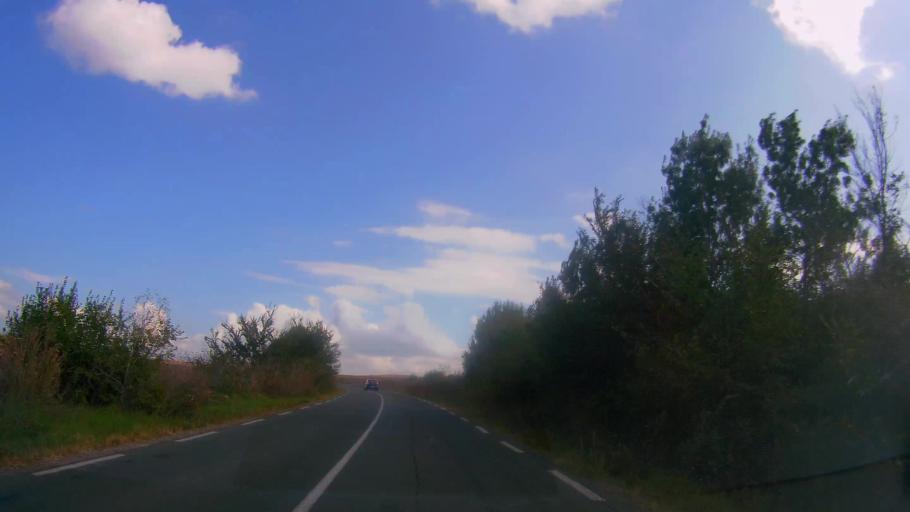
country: BG
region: Burgas
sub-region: Obshtina Kameno
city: Kameno
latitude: 42.4791
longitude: 27.3479
